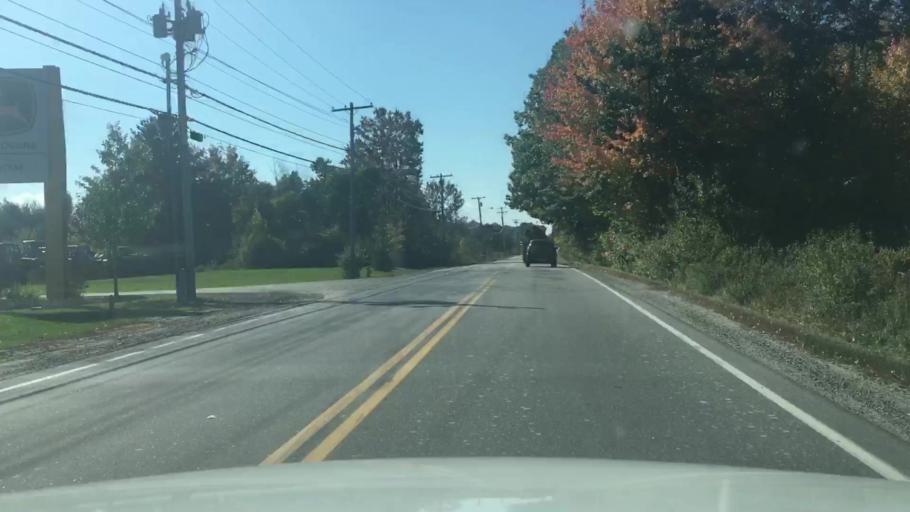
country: US
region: Maine
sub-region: Cumberland County
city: Westbrook
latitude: 43.6506
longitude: -70.3614
